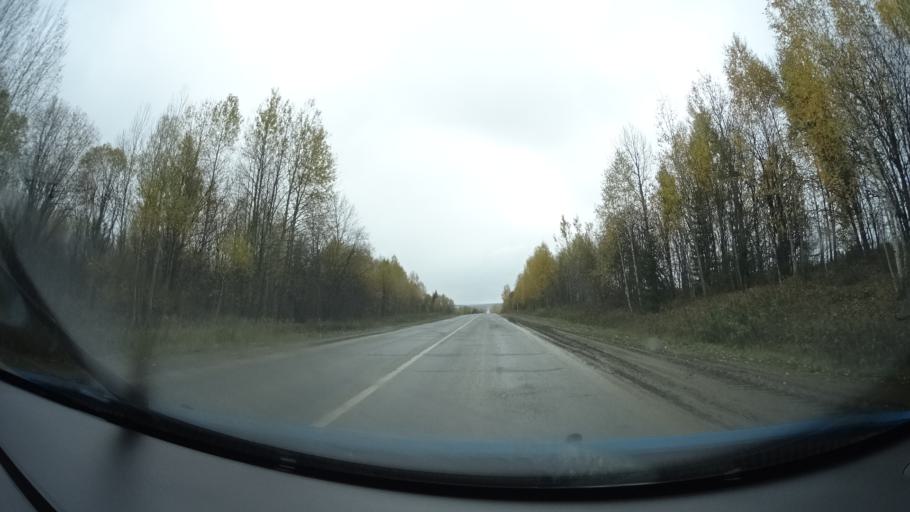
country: RU
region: Perm
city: Chernushka
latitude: 56.7568
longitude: 56.1444
